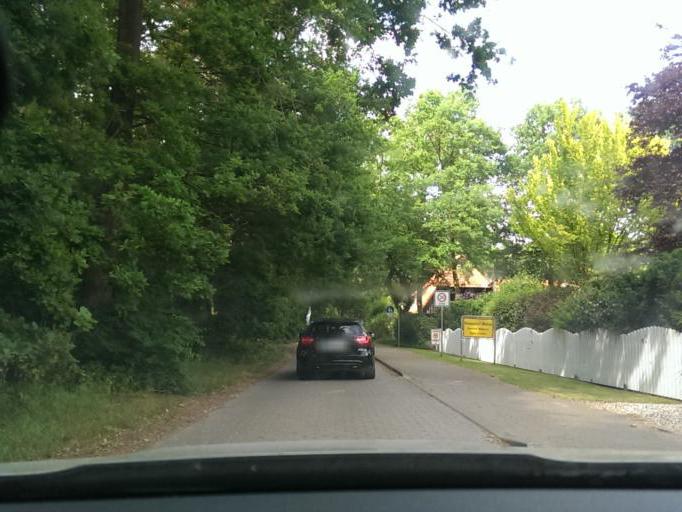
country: DE
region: Lower Saxony
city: Langenhagen
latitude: 52.5014
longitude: 9.7727
